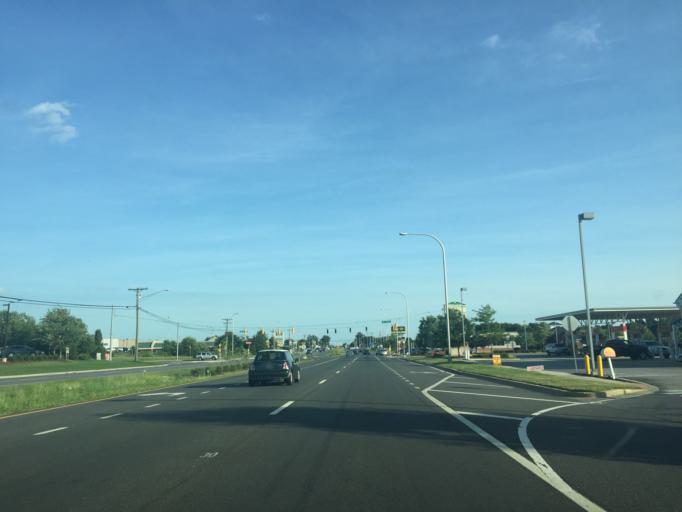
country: US
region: Delaware
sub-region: Kent County
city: Smyrna
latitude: 39.2831
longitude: -75.5938
